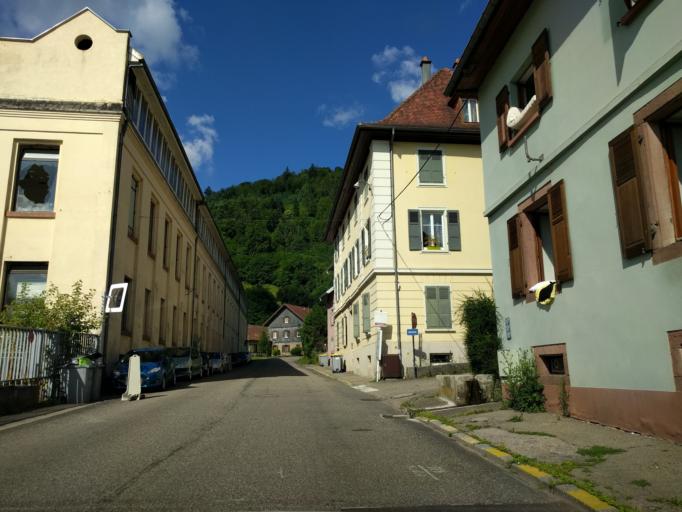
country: FR
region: Alsace
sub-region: Departement du Haut-Rhin
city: Sainte-Marie-aux-Mines
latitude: 48.2427
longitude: 7.1678
